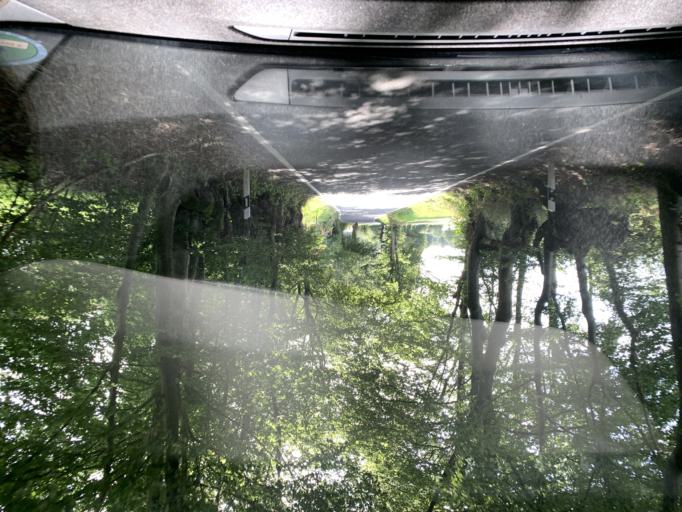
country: DE
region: North Rhine-Westphalia
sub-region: Regierungsbezirk Koln
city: Simmerath
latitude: 50.6020
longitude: 6.2663
